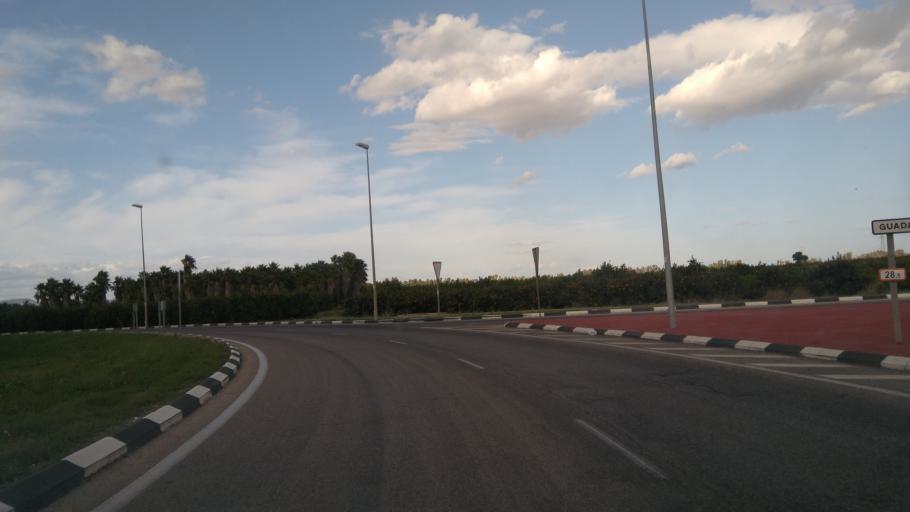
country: ES
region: Valencia
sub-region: Provincia de Valencia
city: L'Alcudia
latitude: 39.1928
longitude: -0.4930
